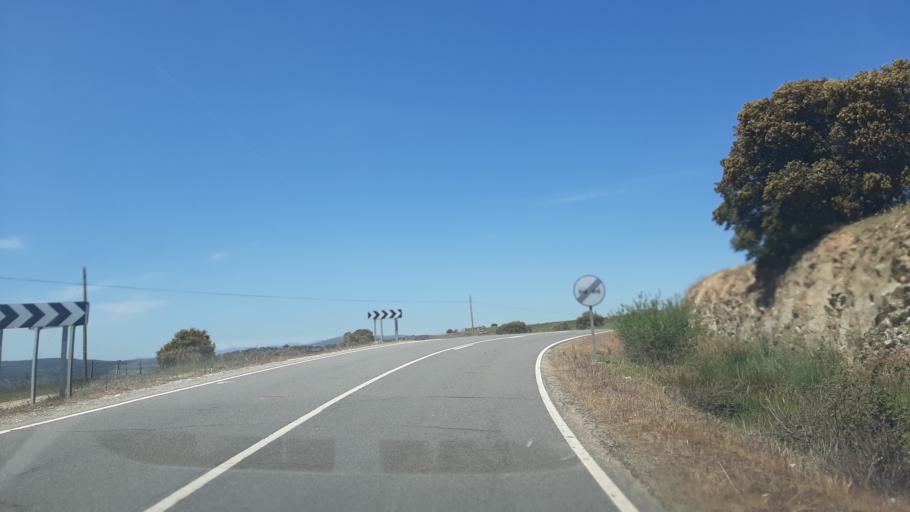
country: ES
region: Castille and Leon
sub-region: Provincia de Salamanca
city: Puente del Congosto
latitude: 40.5324
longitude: -5.5605
